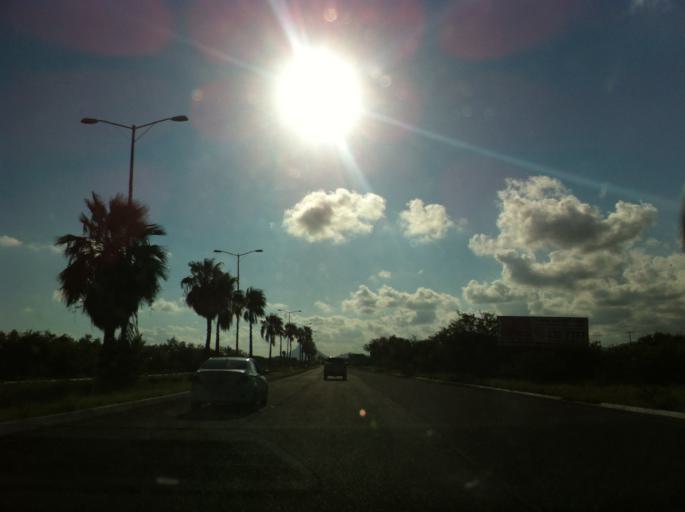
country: MX
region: Sonora
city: Heroica Guaymas
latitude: 27.9805
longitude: -110.9656
